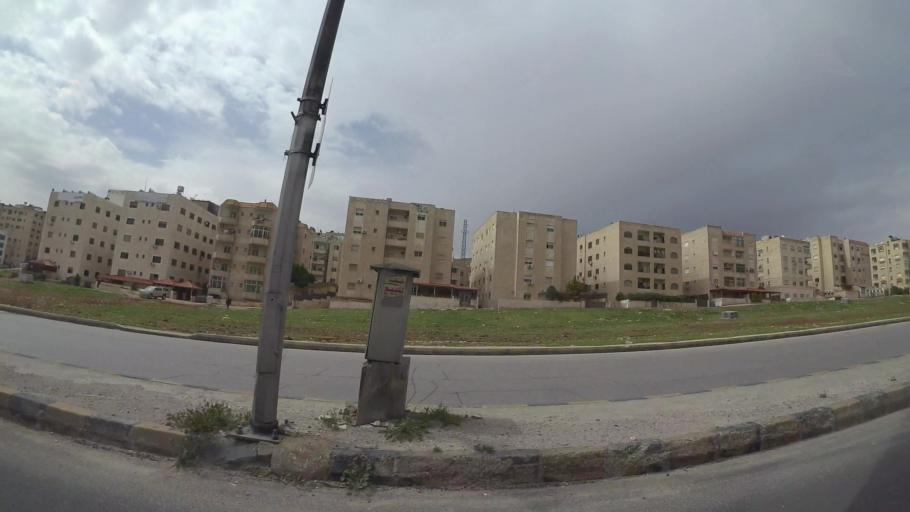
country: JO
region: Amman
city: Amman
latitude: 31.9843
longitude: 35.9180
